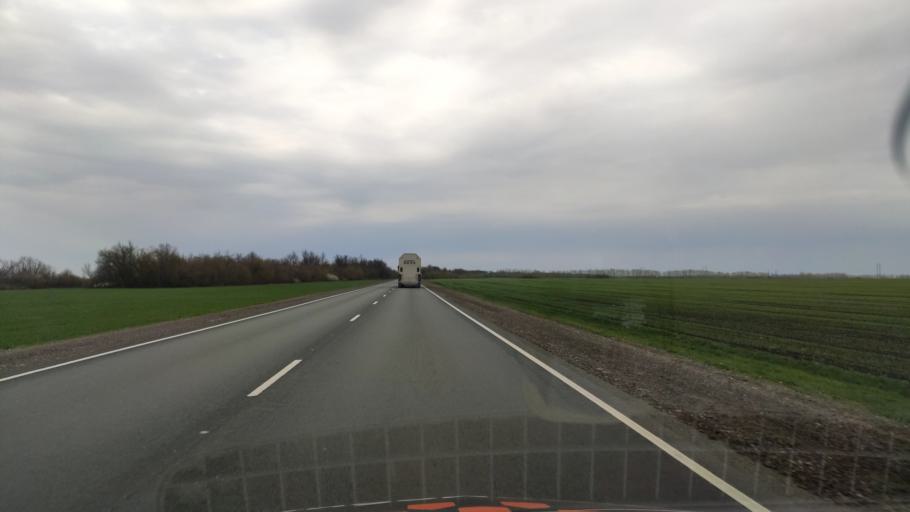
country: RU
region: Voronezj
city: Nizhnedevitsk
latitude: 51.6053
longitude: 38.6074
